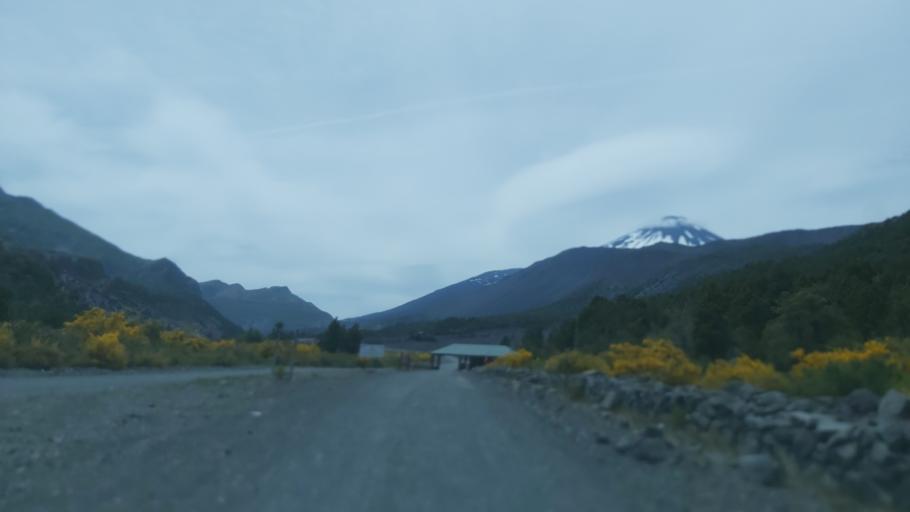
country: AR
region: Neuquen
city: Andacollo
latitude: -37.3984
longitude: -71.4415
